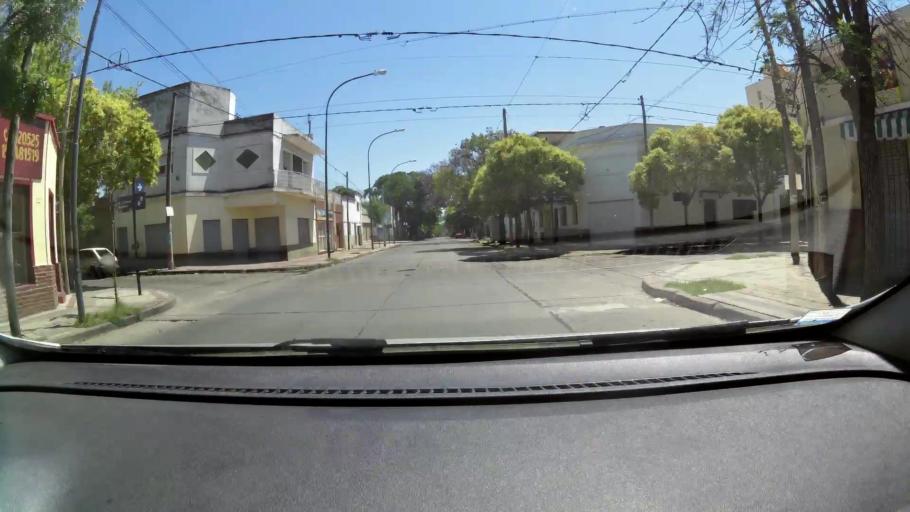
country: AR
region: Cordoba
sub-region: Departamento de Capital
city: Cordoba
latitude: -31.4217
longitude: -64.2011
